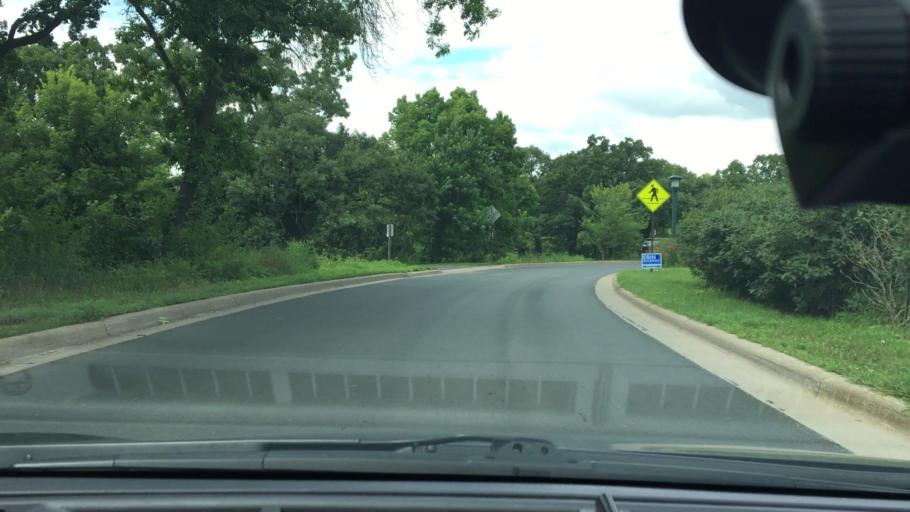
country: US
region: Minnesota
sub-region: Dakota County
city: Mendota Heights
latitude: 44.9158
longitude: -93.2069
